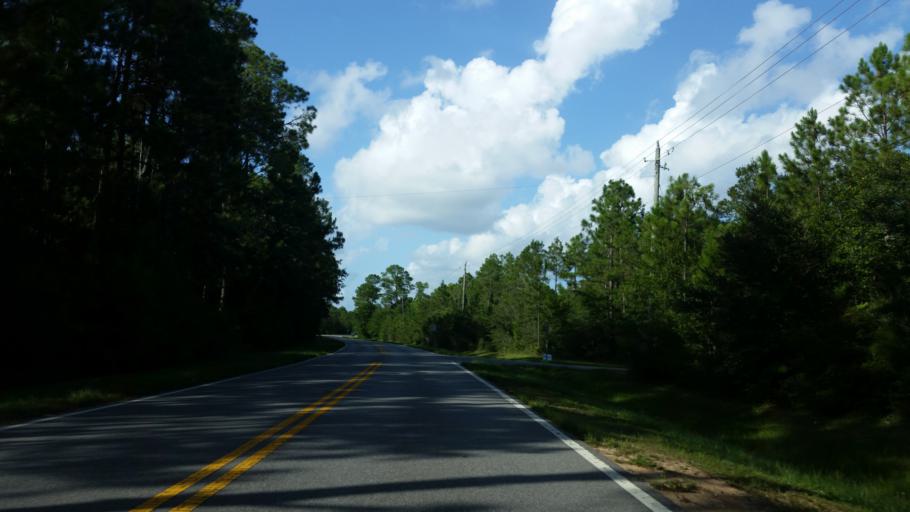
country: US
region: Florida
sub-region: Santa Rosa County
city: Bagdad
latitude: 30.4947
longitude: -87.0637
